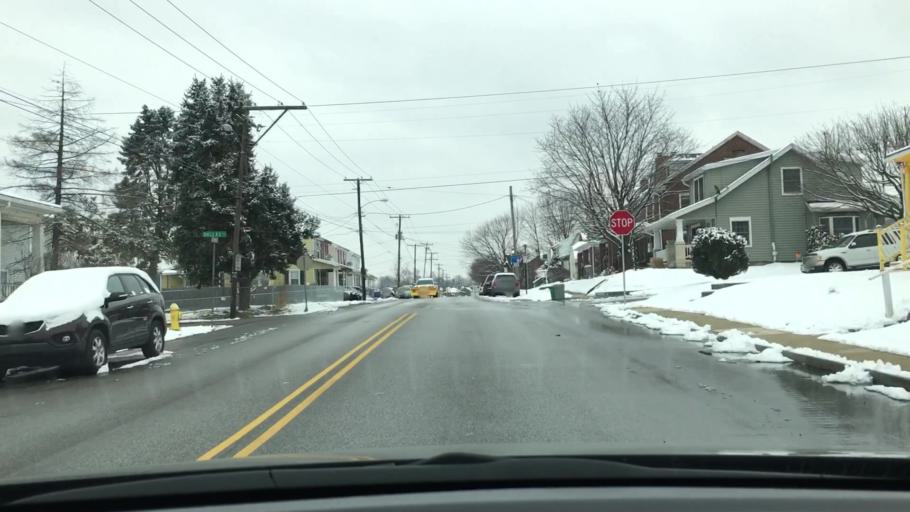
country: US
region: Pennsylvania
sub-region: York County
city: Valley View
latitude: 39.9584
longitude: -76.7081
